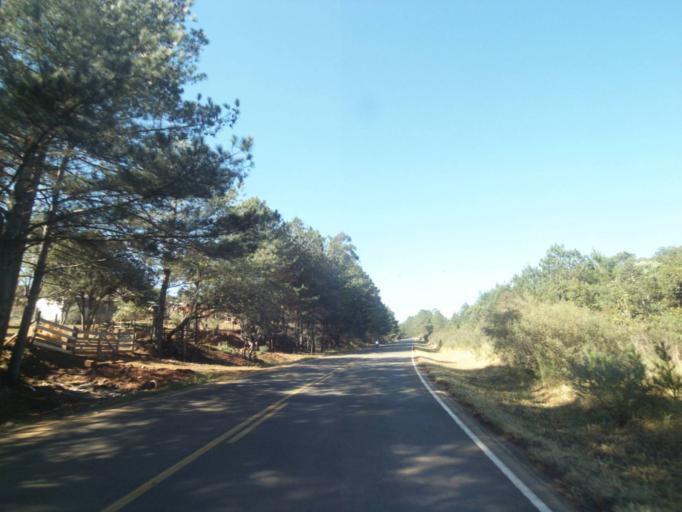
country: BR
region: Parana
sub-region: Tibagi
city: Tibagi
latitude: -24.4751
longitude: -50.4864
